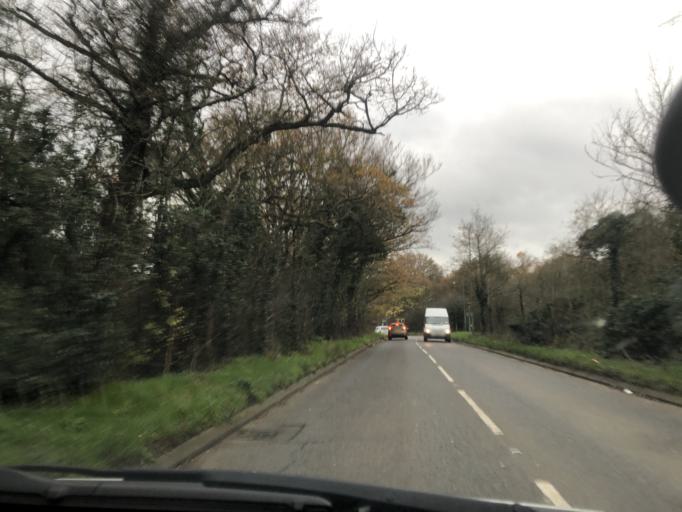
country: GB
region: England
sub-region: Greater London
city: Bexley
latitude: 51.4405
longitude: 0.1821
